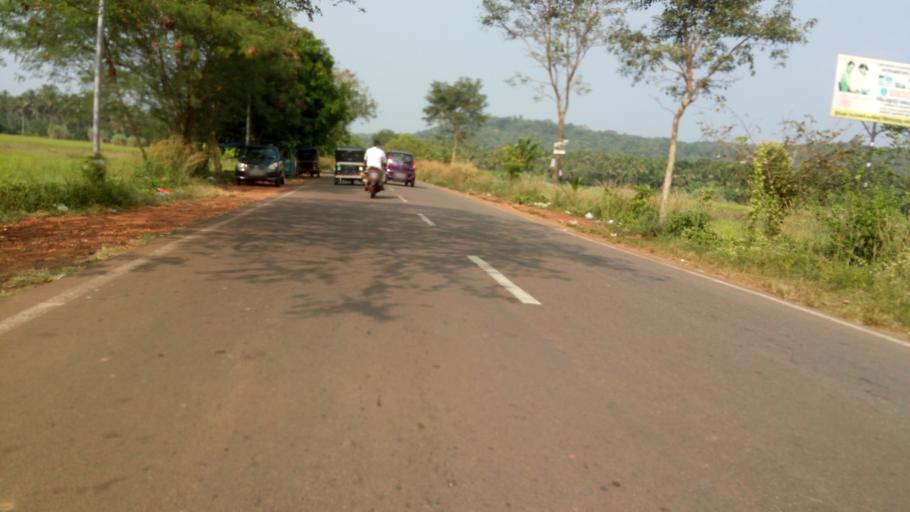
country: IN
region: Kerala
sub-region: Malappuram
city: Malappuram
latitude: 10.9949
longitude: 76.0142
